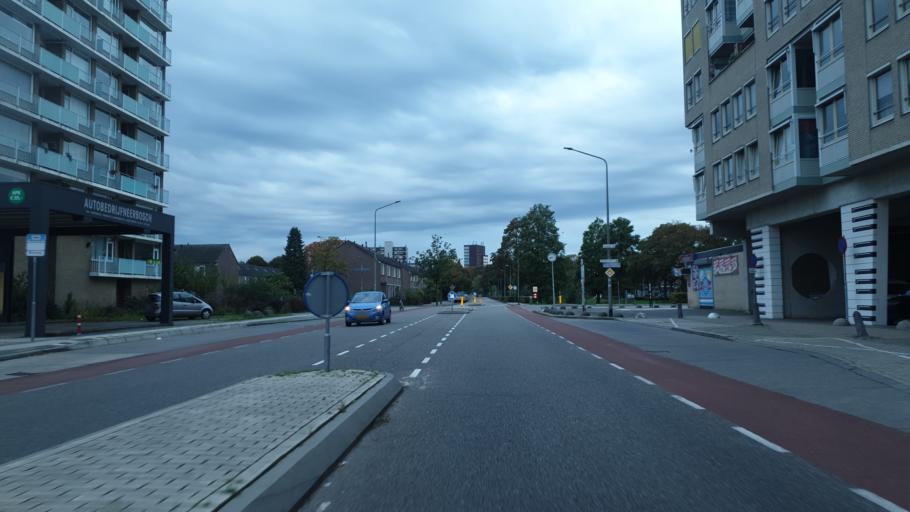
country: NL
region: Gelderland
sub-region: Gemeente Nijmegen
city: Lindenholt
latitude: 51.8301
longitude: 5.8148
